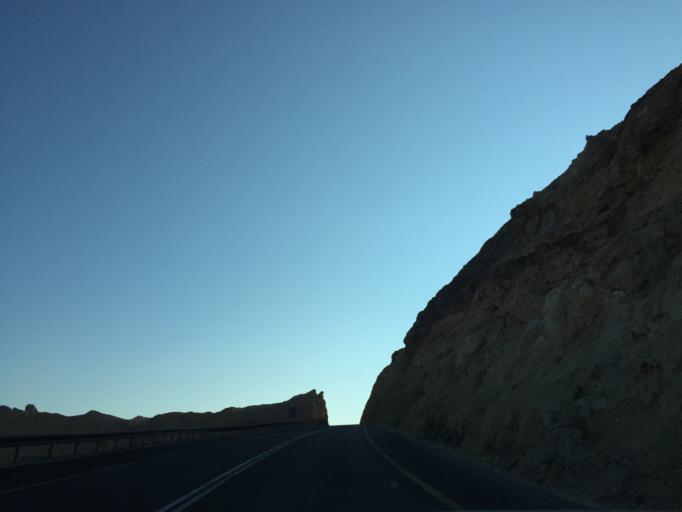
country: IL
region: Southern District
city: Mitzpe Ramon
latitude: 30.3207
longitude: 34.9625
